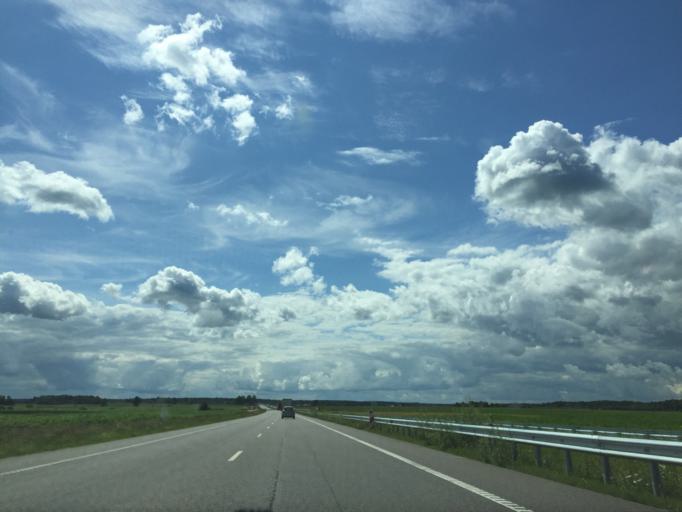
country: LT
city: Kazlu Ruda
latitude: 54.6993
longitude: 23.6114
